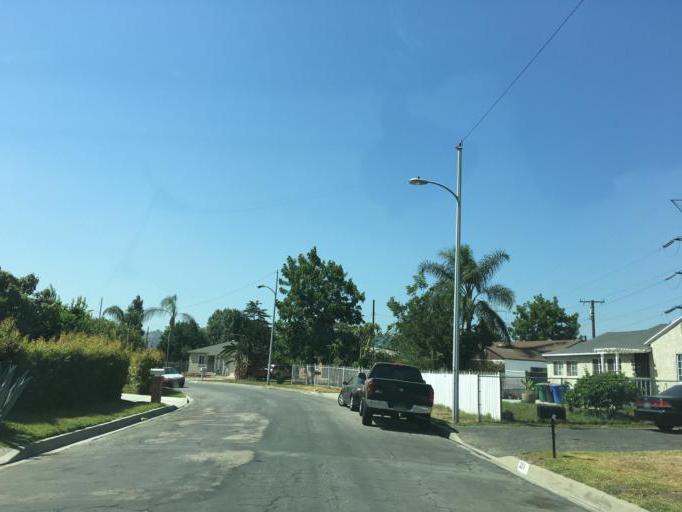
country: US
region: California
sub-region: Los Angeles County
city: Avocado Heights
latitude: 34.0517
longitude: -118.0045
